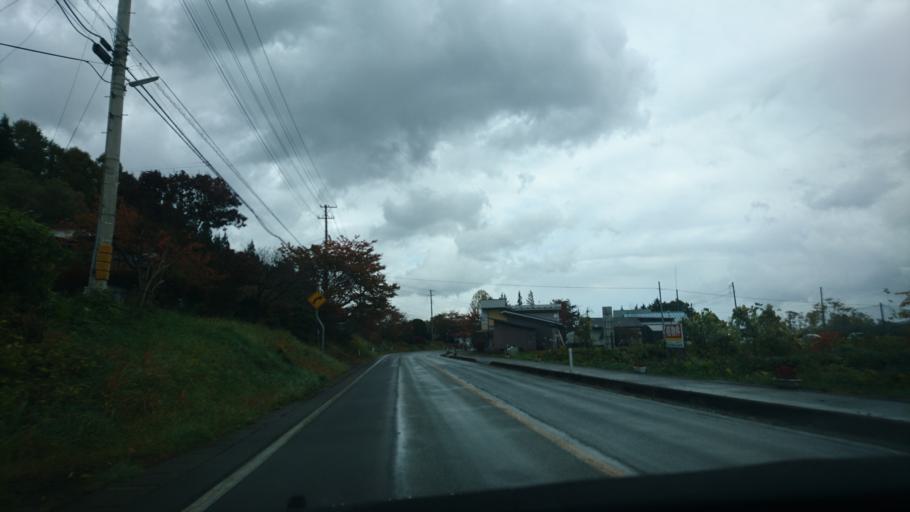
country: JP
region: Iwate
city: Shizukuishi
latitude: 39.6710
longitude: 140.9827
